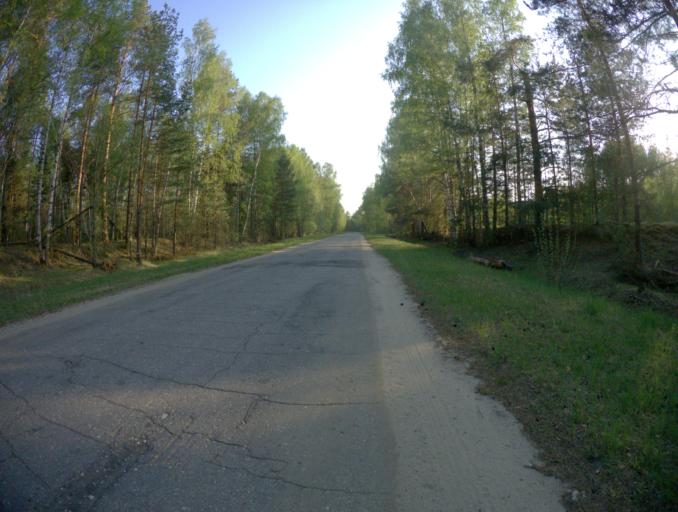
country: RU
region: Vladimir
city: Vyazniki
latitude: 56.3324
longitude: 42.1266
